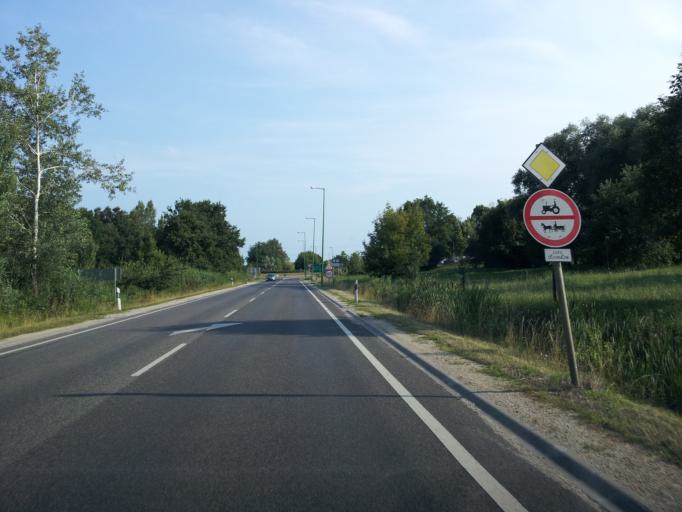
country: HU
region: Veszprem
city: Liter
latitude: 47.0756
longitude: 18.0354
